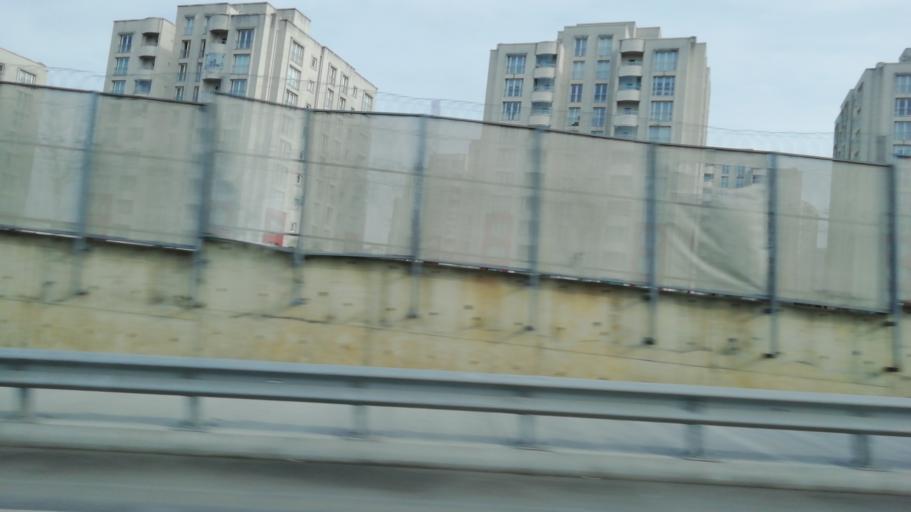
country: TR
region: Istanbul
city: Basaksehir
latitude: 41.1213
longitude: 28.7984
